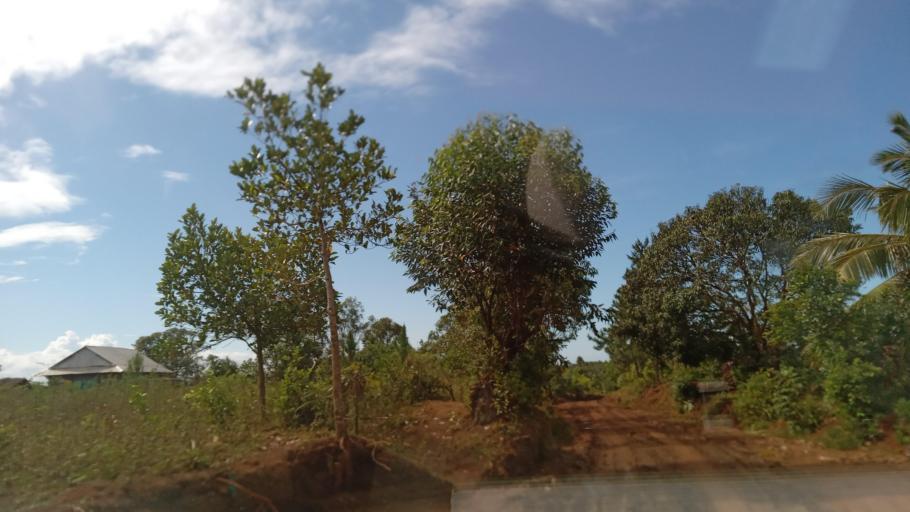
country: MG
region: Atsimo-Atsinanana
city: Vohipaho
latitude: -23.7321
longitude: 47.5628
